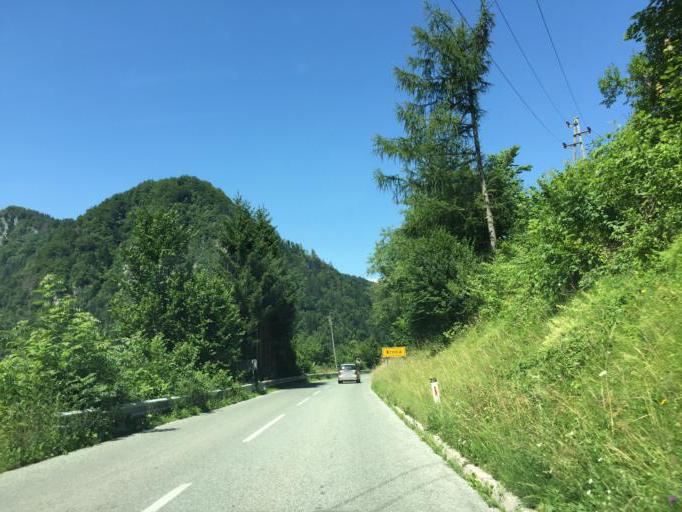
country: SI
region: Gorje
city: Zgornje Gorje
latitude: 46.3751
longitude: 14.0556
